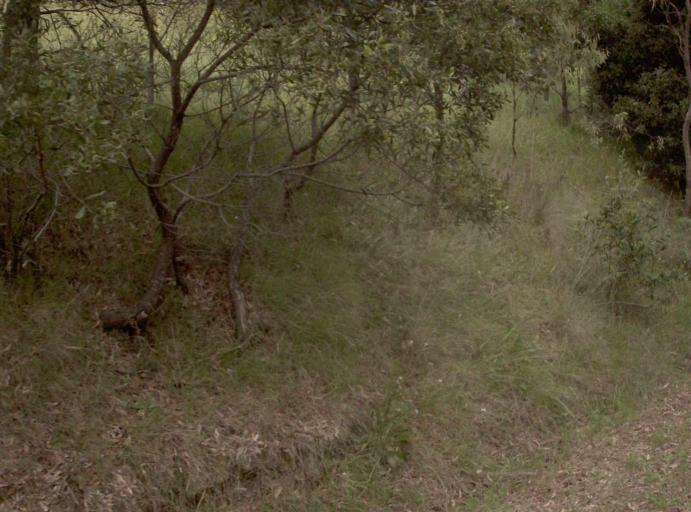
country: AU
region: Victoria
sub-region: East Gippsland
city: Bairnsdale
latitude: -37.5746
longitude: 147.1853
